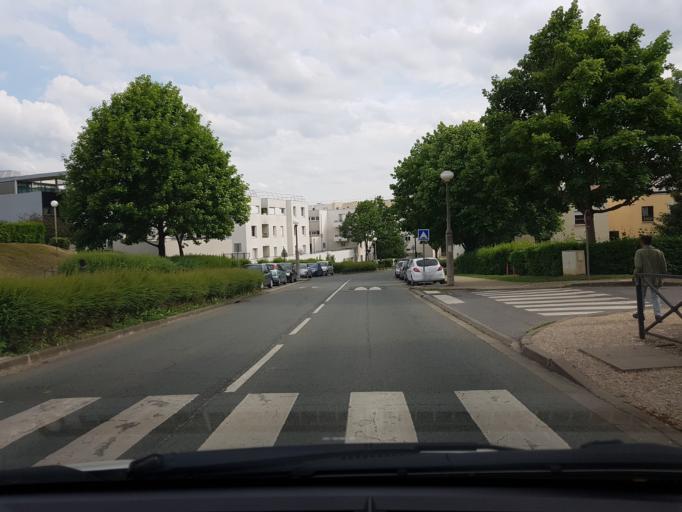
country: FR
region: Ile-de-France
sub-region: Departement de Seine-et-Marne
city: Torcy
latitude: 48.8413
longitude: 2.6509
